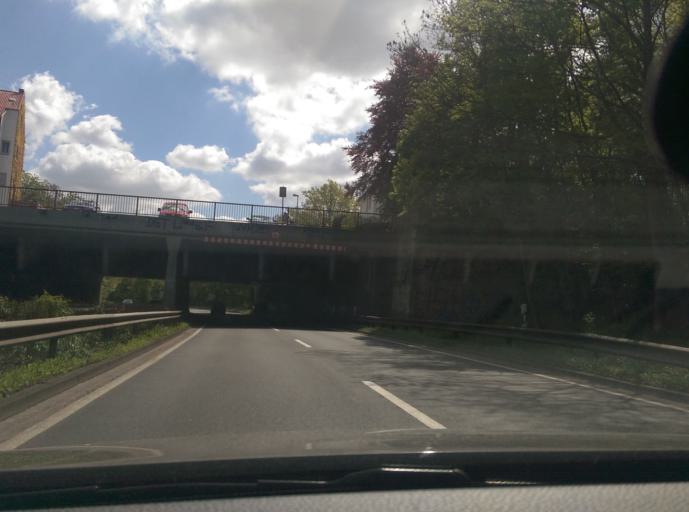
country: DE
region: Lower Saxony
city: Hannover
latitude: 52.3647
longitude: 9.7060
